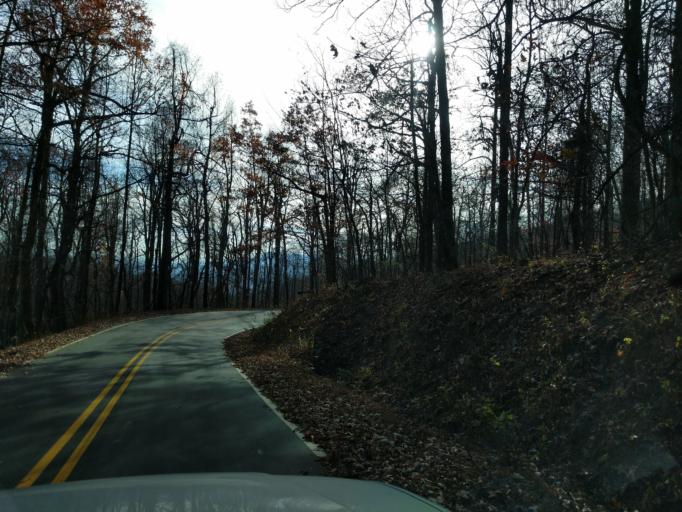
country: US
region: North Carolina
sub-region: Polk County
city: Columbus
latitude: 35.2756
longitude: -82.2276
